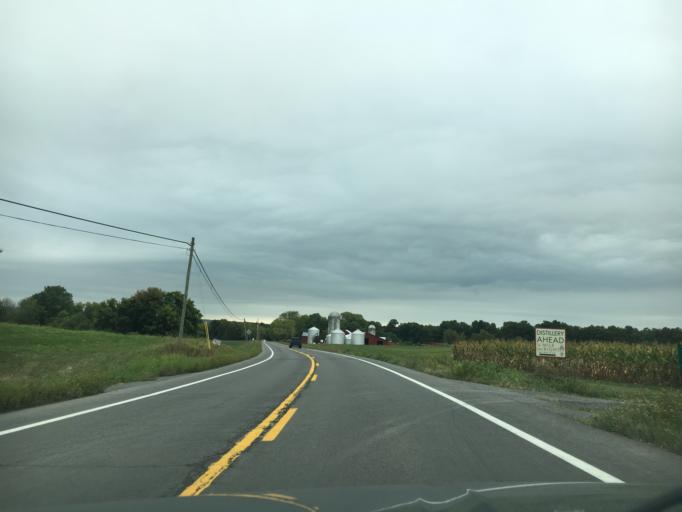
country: US
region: New York
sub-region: Tompkins County
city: Trumansburg
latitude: 42.6720
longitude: -76.7380
